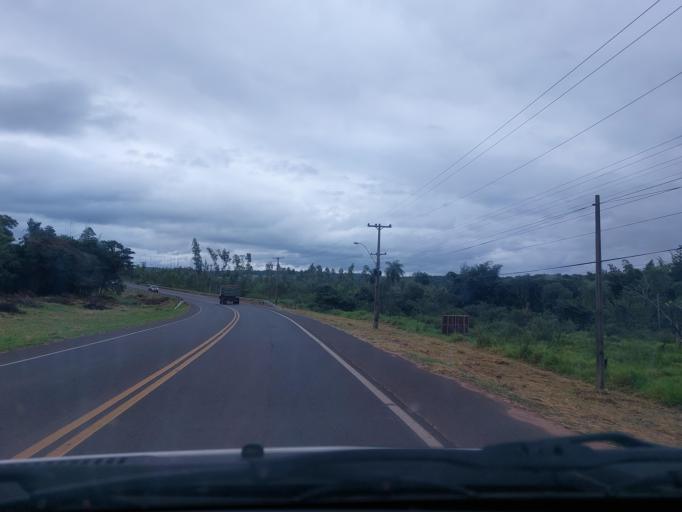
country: PY
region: San Pedro
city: Guayaybi
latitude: -24.6676
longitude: -56.4123
